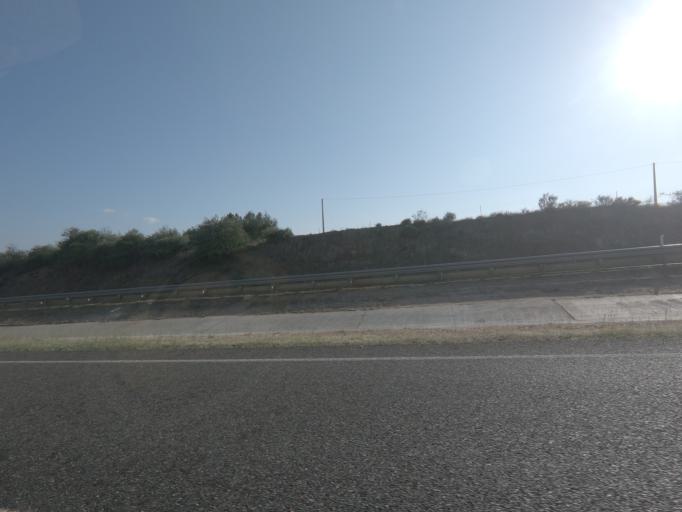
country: ES
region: Galicia
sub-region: Provincia de Ourense
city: Oimbra
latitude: 41.8495
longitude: -7.4127
